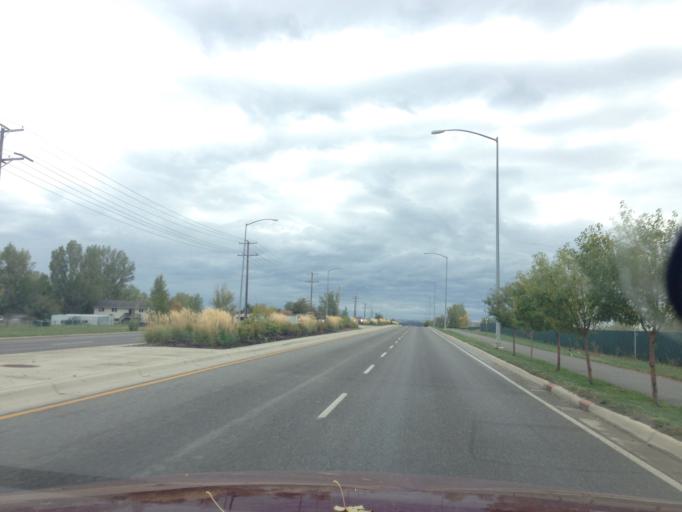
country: US
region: Montana
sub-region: Yellowstone County
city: Billings
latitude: 45.7459
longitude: -108.6176
